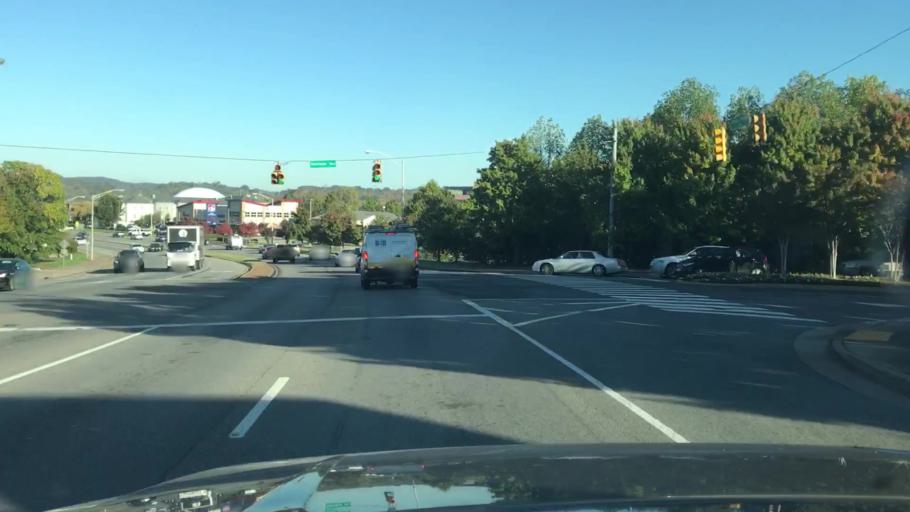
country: US
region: Tennessee
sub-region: Davidson County
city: Nashville
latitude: 36.1908
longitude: -86.7987
